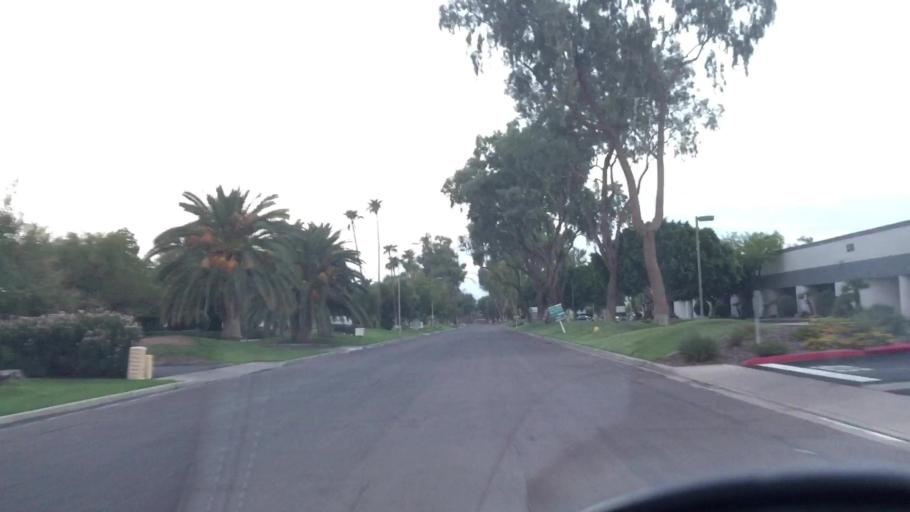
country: US
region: Arizona
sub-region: Maricopa County
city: Tempe Junction
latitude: 33.4098
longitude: -111.9633
